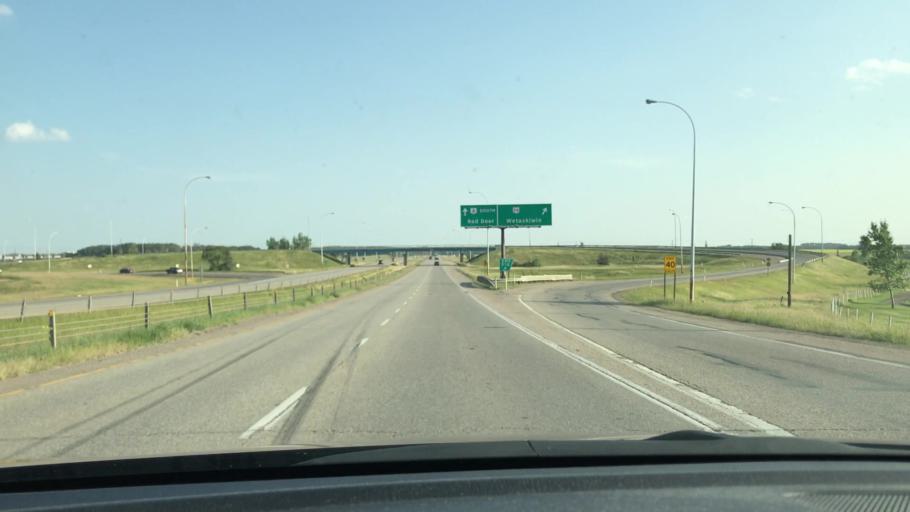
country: CA
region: Alberta
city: Leduc
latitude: 53.2556
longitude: -113.5618
